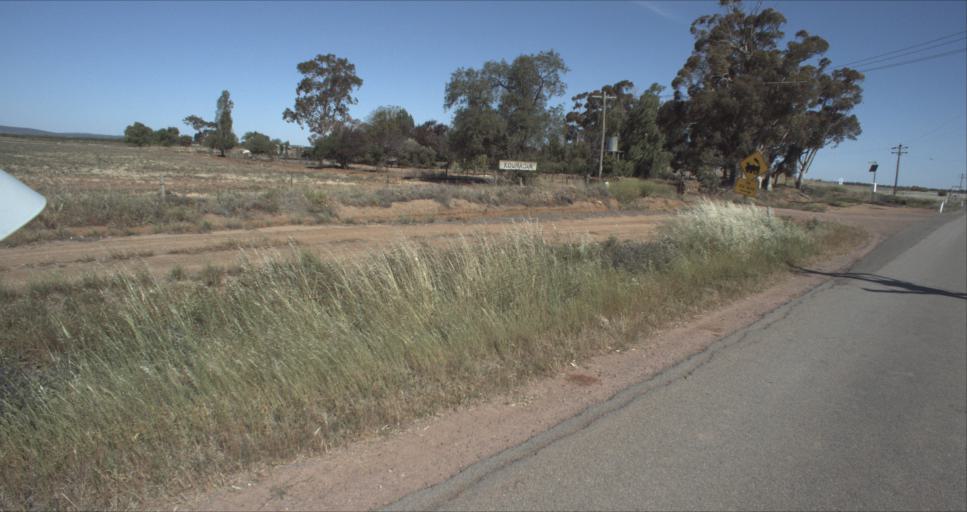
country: AU
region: New South Wales
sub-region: Leeton
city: Leeton
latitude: -34.4772
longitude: 146.3681
